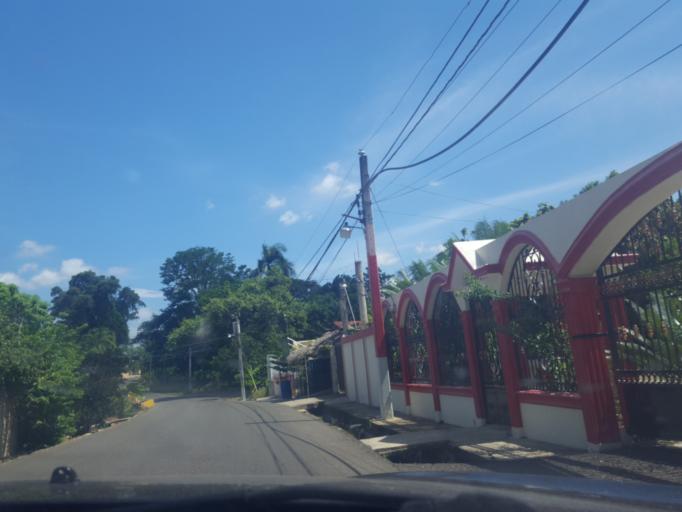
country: DO
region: Santiago
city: Baitoa
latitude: 19.3786
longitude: -70.6518
